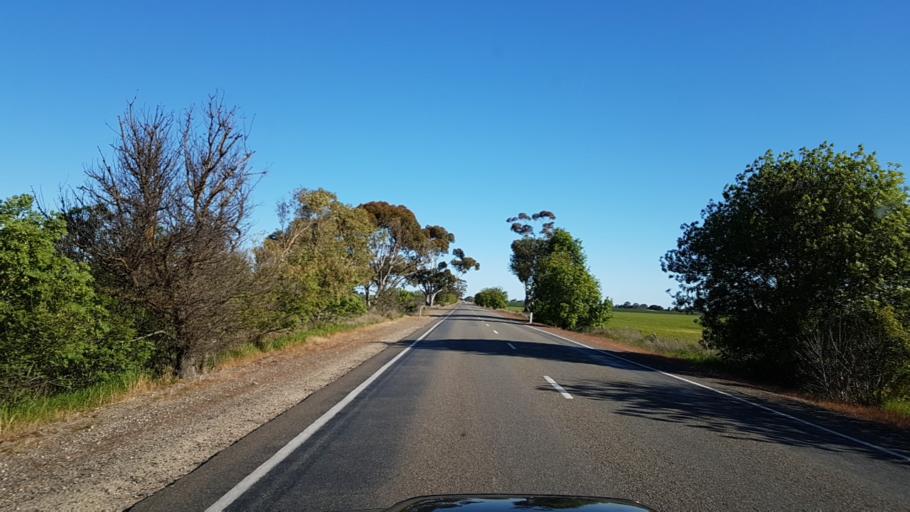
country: AU
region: South Australia
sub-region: Light
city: Kapunda
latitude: -34.1794
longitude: 138.7450
